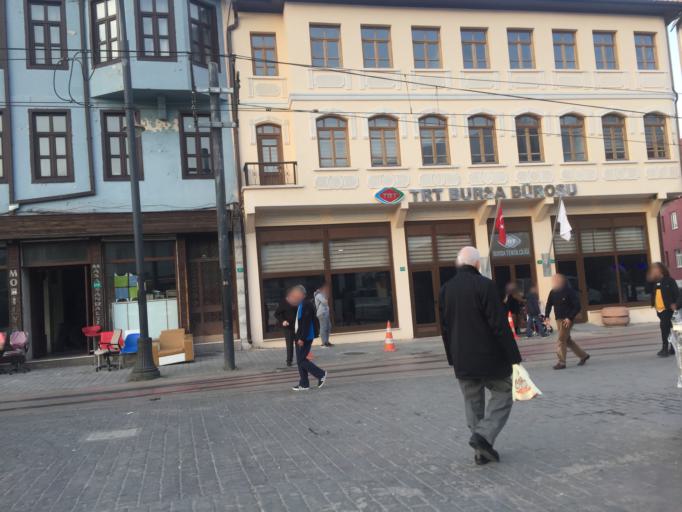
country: TR
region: Bursa
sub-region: Osmangazi
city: Bursa
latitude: 40.1849
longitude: 29.0714
